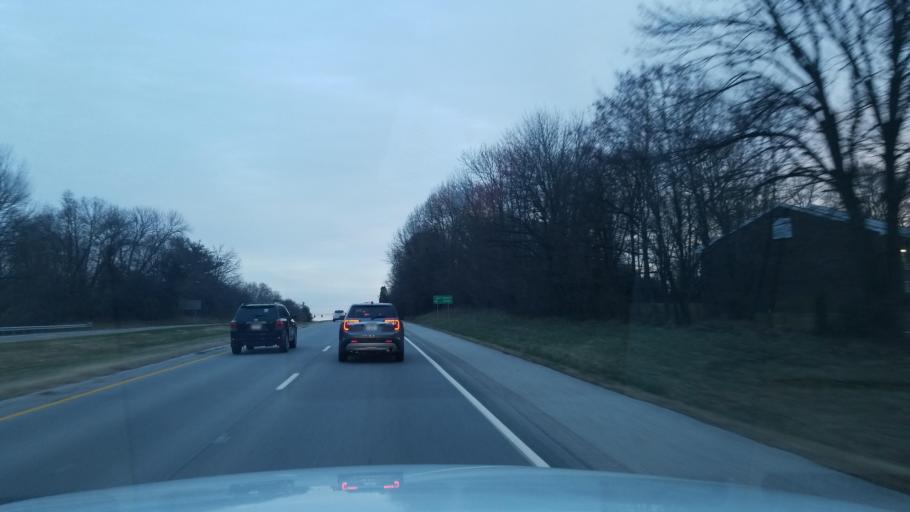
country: US
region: Indiana
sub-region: Vanderburgh County
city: Evansville
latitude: 37.9686
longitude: -87.6684
